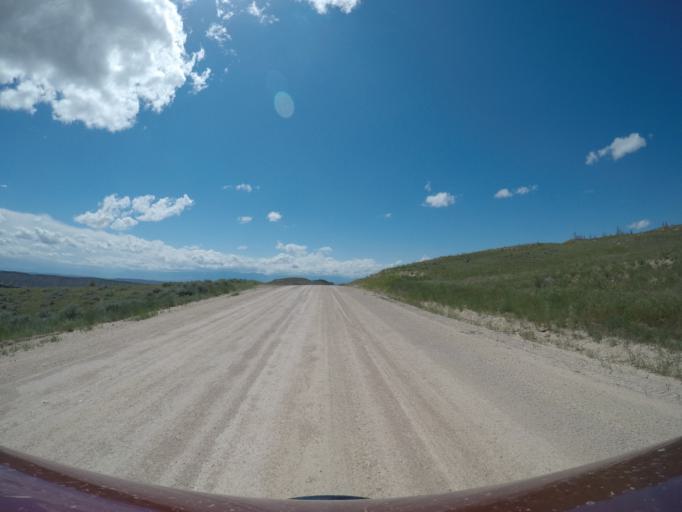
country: US
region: Wyoming
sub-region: Park County
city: Powell
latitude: 45.2067
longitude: -108.7856
